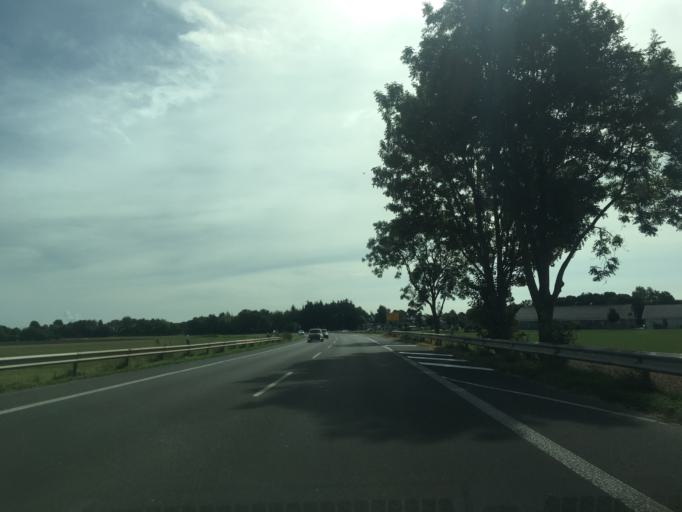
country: DE
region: North Rhine-Westphalia
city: Erkelenz
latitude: 51.0667
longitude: 6.3377
